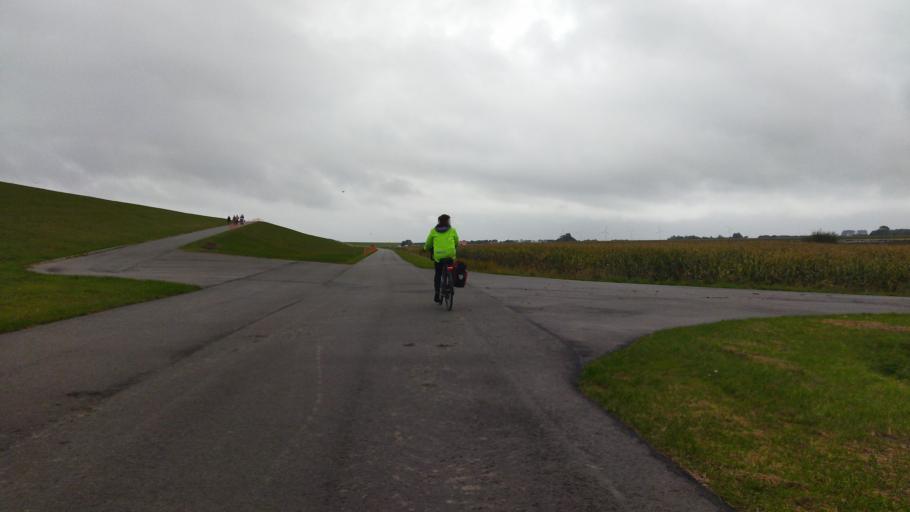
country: NL
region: Groningen
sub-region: Gemeente Delfzijl
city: Delfzijl
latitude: 53.4078
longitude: 7.0150
